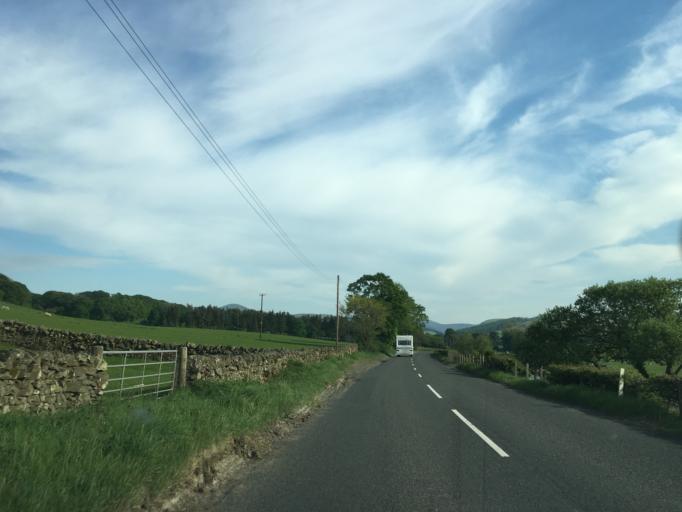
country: GB
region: Scotland
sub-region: South Lanarkshire
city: Biggar
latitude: 55.6257
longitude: -3.4159
